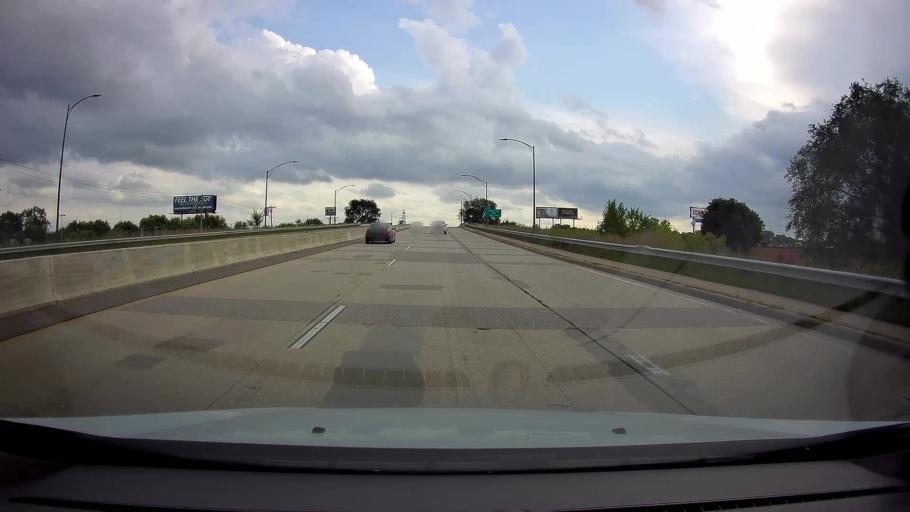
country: US
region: Minnesota
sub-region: Ramsey County
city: Falcon Heights
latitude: 44.9751
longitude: -93.1671
